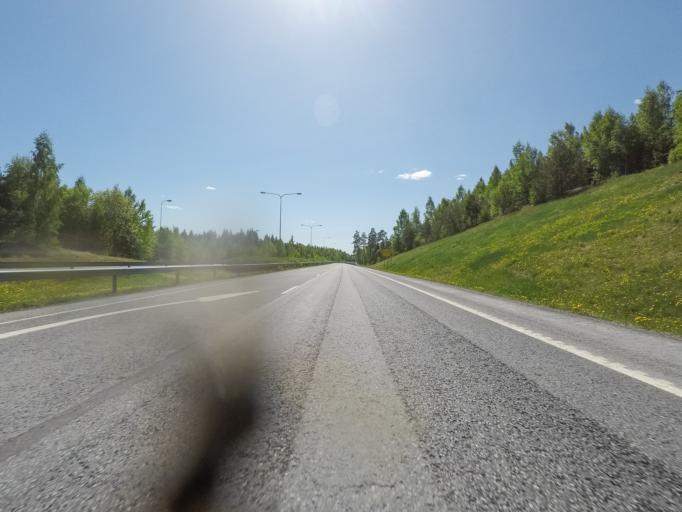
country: FI
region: Pirkanmaa
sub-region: Etelae-Pirkanmaa
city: Toijala
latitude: 61.1928
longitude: 23.8117
